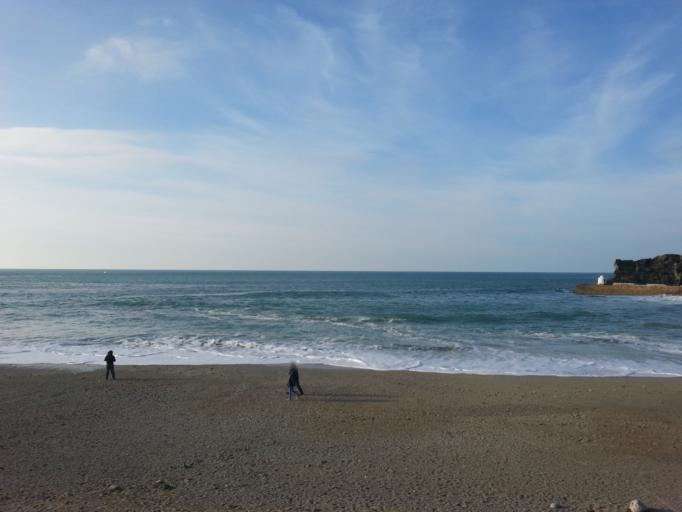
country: GB
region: England
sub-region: Cornwall
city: Camborne
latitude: 50.2613
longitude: -5.2928
